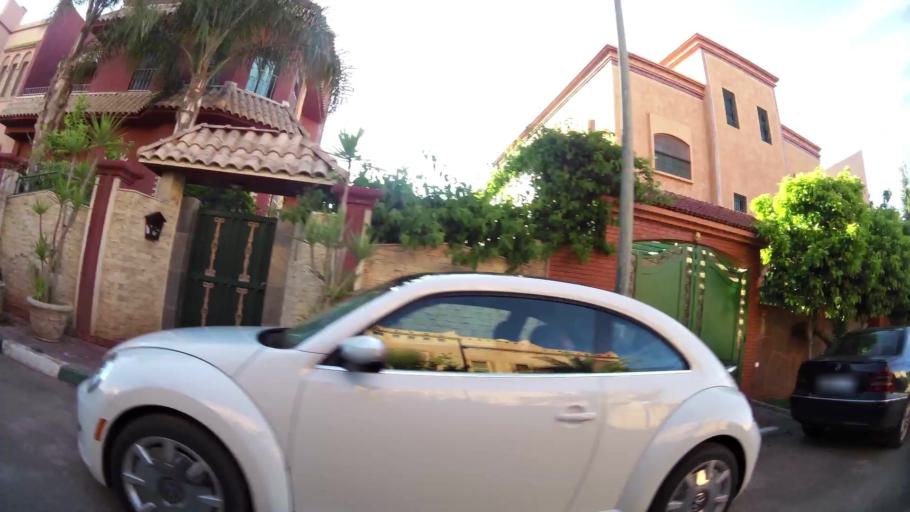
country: MA
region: Marrakech-Tensift-Al Haouz
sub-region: Marrakech
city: Marrakesh
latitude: 31.6628
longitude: -8.0610
